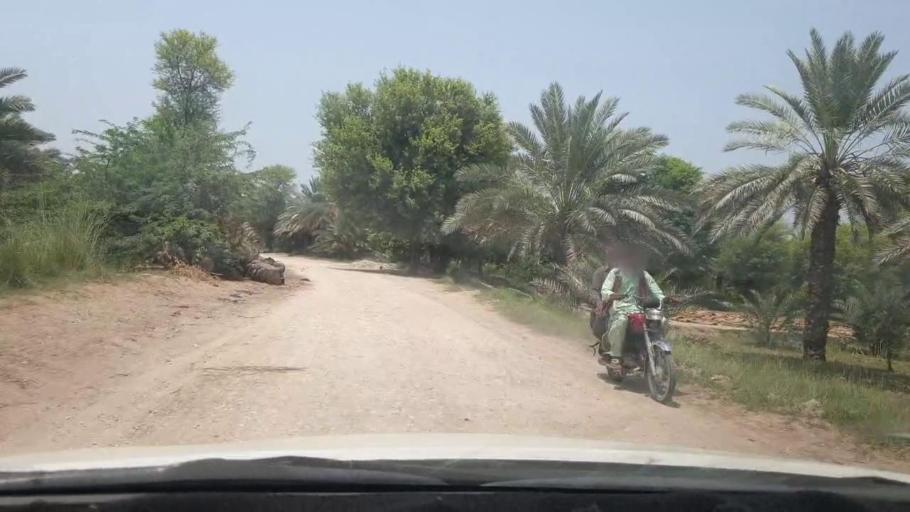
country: PK
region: Sindh
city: Khairpur
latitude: 27.5010
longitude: 68.8730
